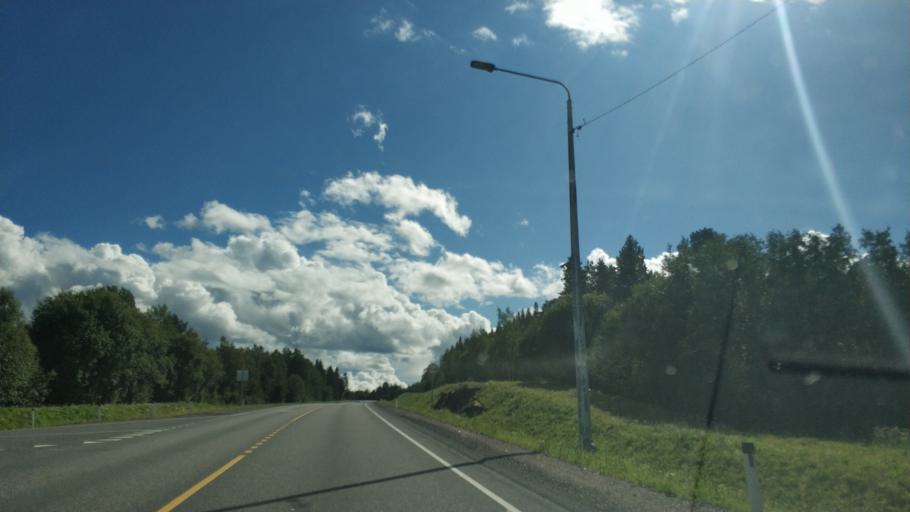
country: RU
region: Republic of Karelia
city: Ruskeala
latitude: 61.9016
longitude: 30.6349
